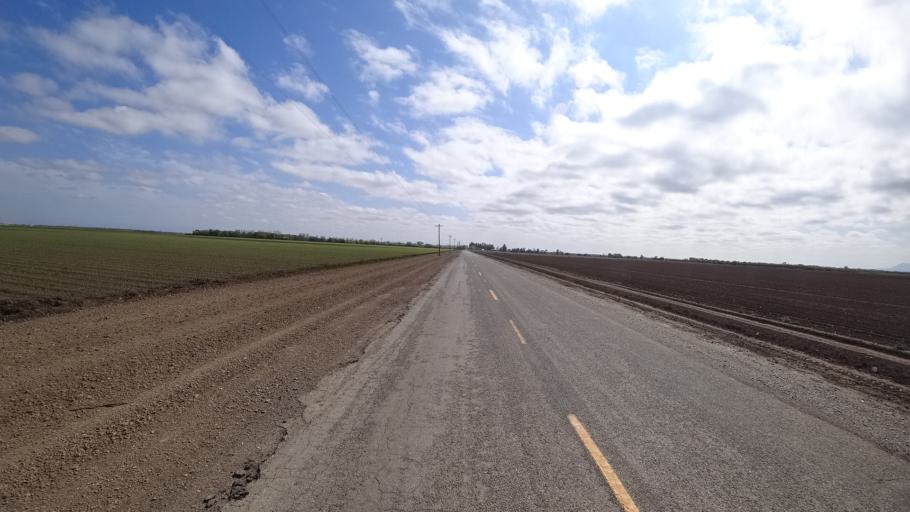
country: US
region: California
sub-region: Colusa County
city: Colusa
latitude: 39.4199
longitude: -121.9376
